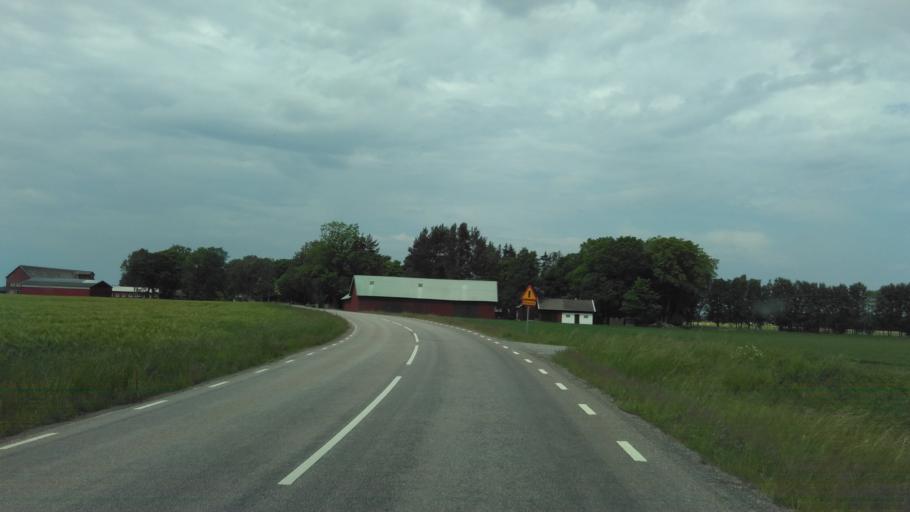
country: SE
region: Vaestra Goetaland
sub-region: Lidkopings Kommun
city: Lidkoping
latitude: 58.4651
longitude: 13.1493
